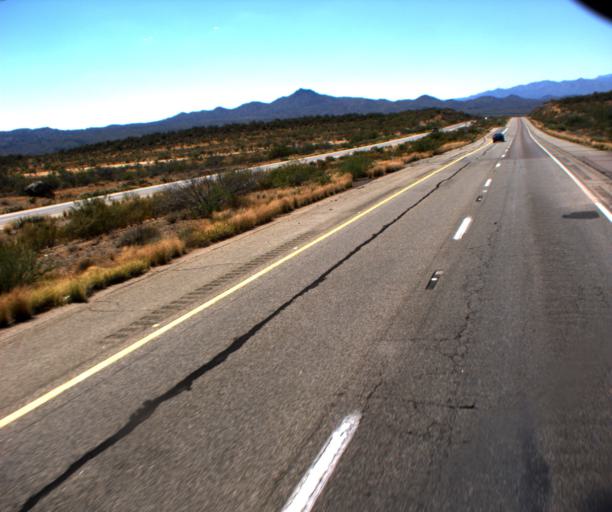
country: US
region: Arizona
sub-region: Yavapai County
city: Bagdad
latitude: 34.4902
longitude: -113.3824
